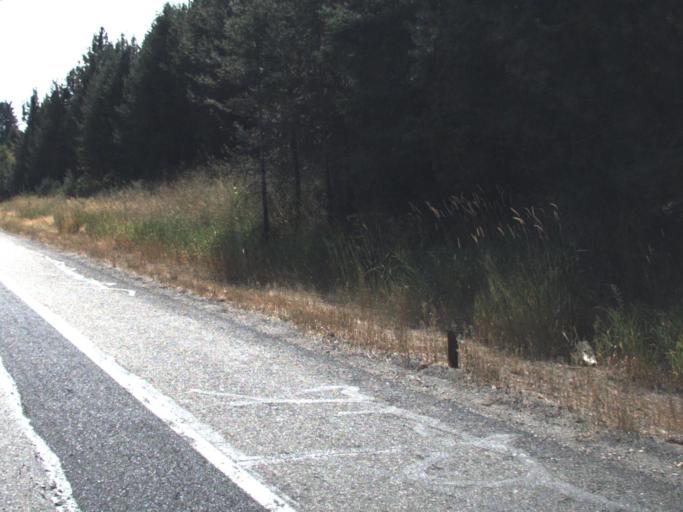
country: US
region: Washington
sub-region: Stevens County
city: Chewelah
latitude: 48.1280
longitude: -117.6525
